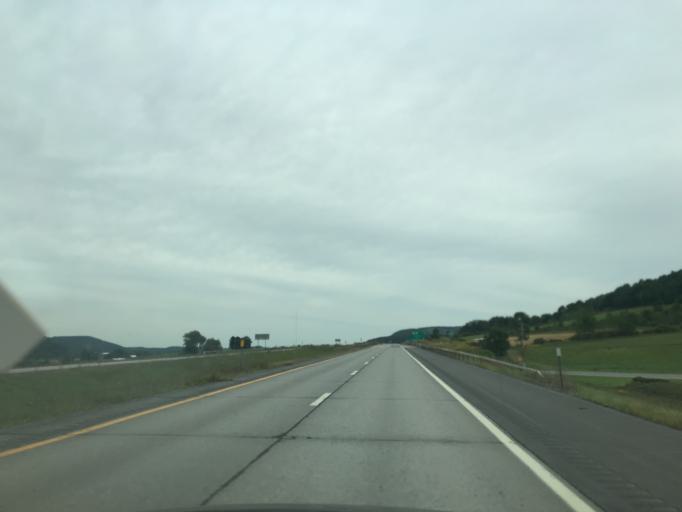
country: US
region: New York
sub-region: Schoharie County
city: Cobleskill
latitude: 42.6450
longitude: -74.5349
